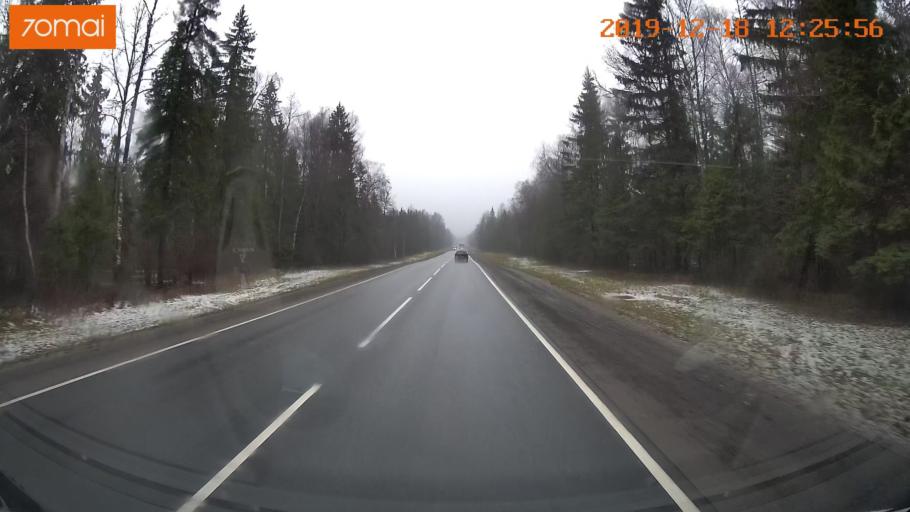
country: RU
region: Moskovskaya
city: Novopetrovskoye
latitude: 56.0450
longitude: 36.4994
